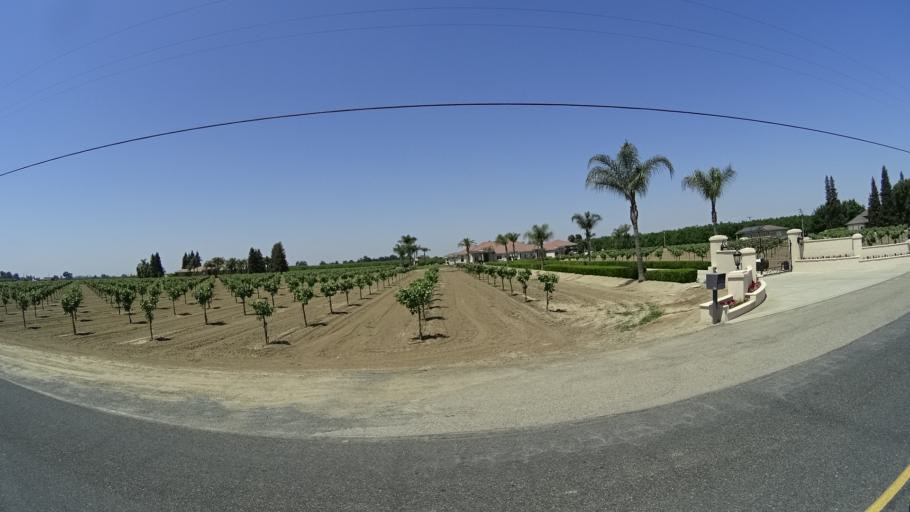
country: US
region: California
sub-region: Fresno County
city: Laton
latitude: 36.4127
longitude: -119.6729
